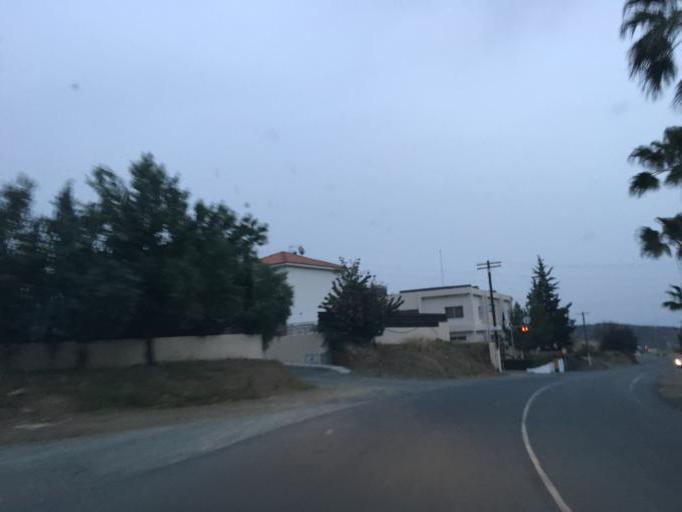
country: CY
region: Limassol
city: Parekklisha
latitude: 34.7372
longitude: 33.1617
